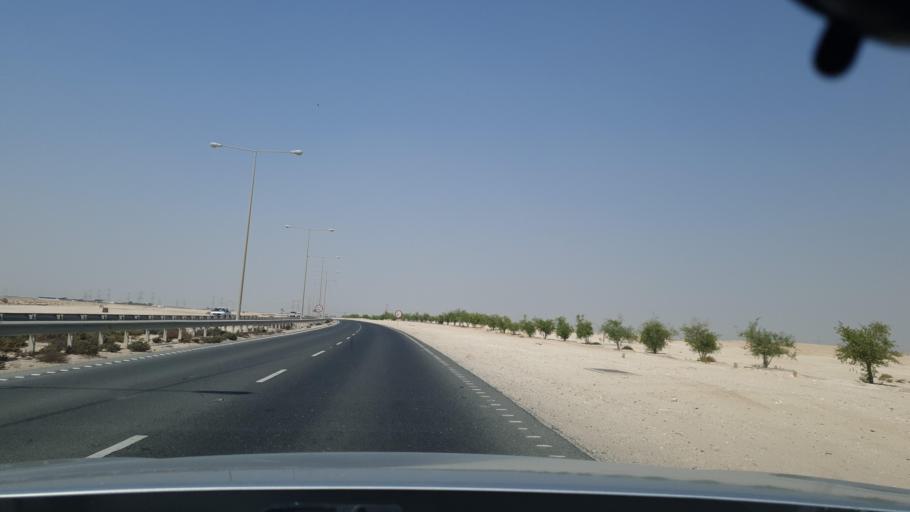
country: QA
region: Al Khawr
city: Al Khawr
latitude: 25.7369
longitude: 51.4910
